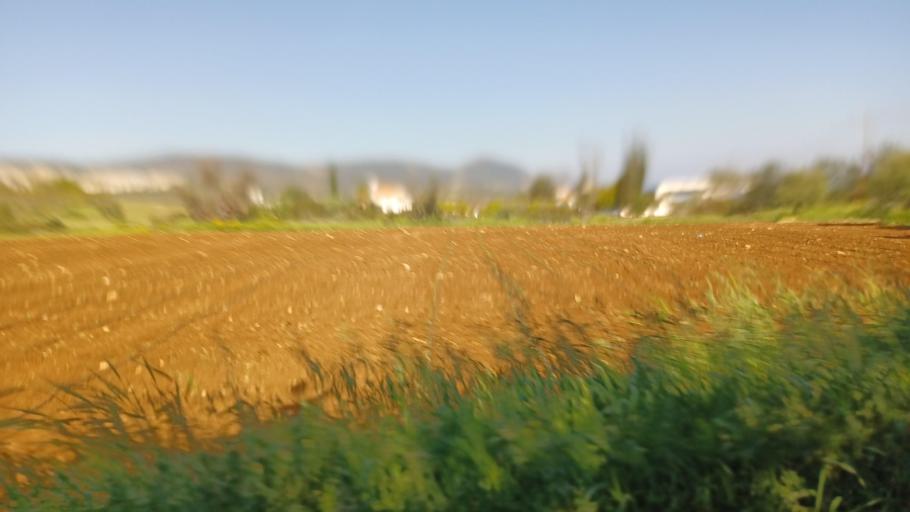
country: CY
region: Pafos
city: Polis
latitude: 35.0296
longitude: 32.3932
